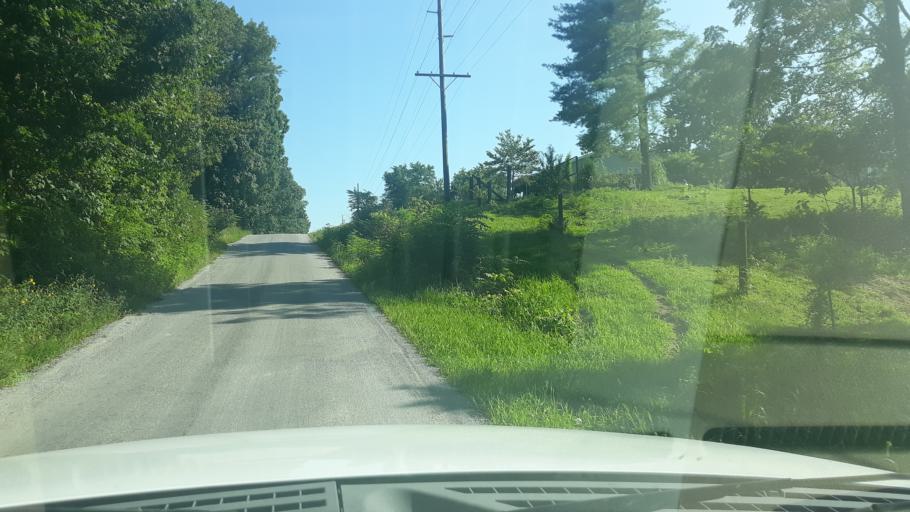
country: US
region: Illinois
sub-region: Saline County
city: Harrisburg
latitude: 37.8535
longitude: -88.5963
